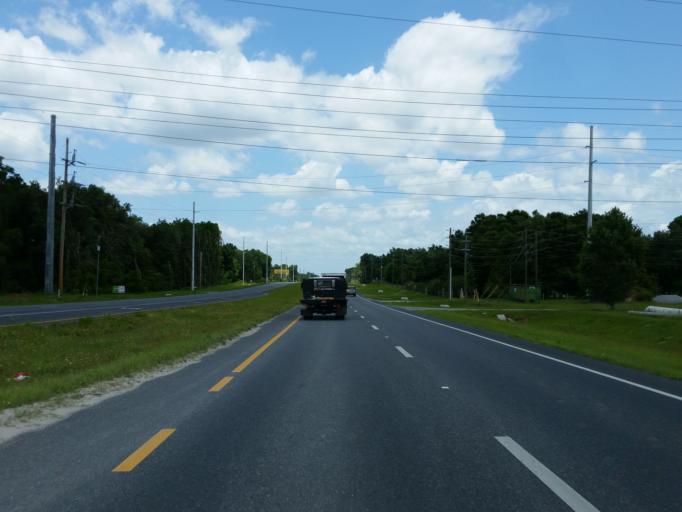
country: US
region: Florida
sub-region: Marion County
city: Belleview
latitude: 28.9701
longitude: -82.0411
